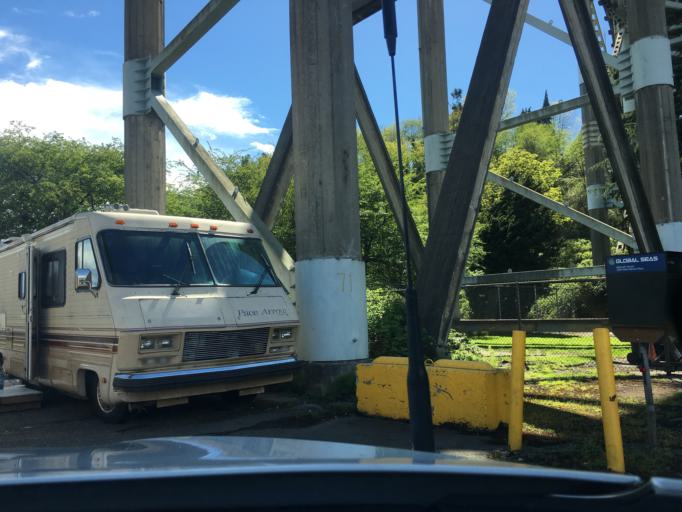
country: US
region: Washington
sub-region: King County
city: Seattle
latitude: 47.6336
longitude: -122.3879
